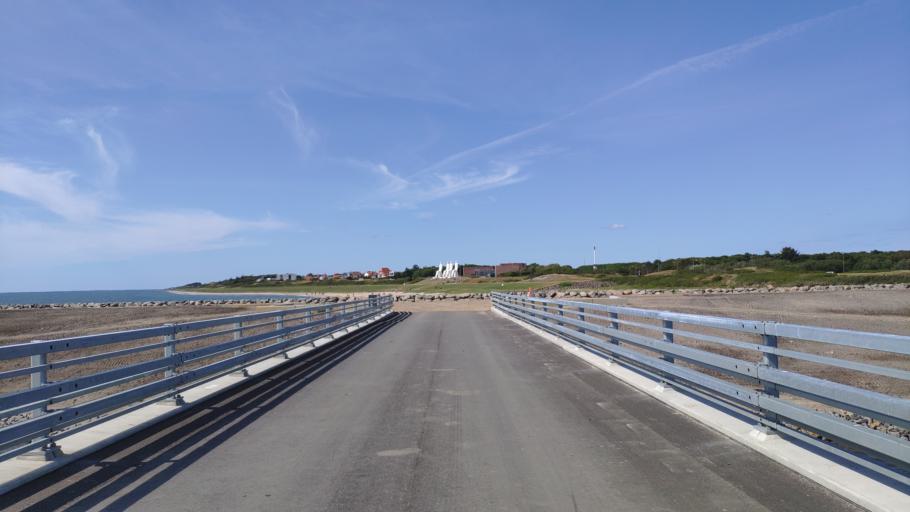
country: DK
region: South Denmark
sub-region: Esbjerg Kommune
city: Esbjerg
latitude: 55.4846
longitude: 8.4132
